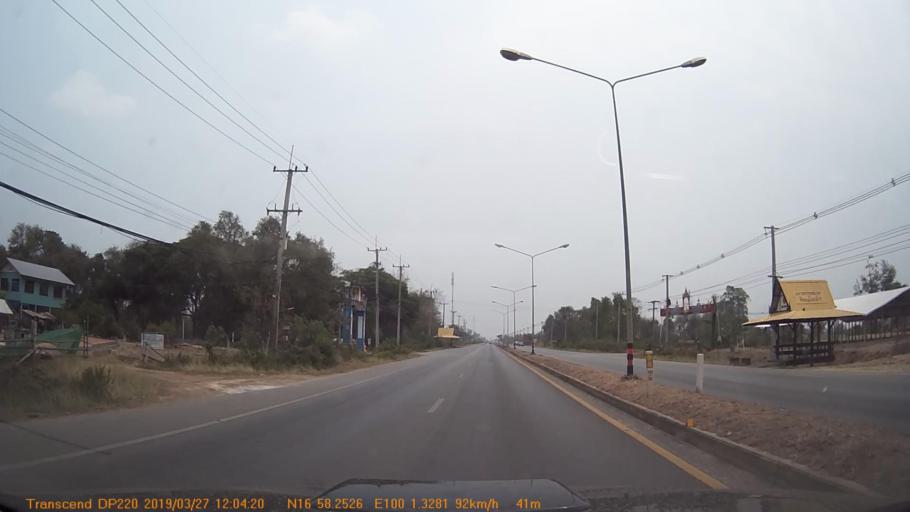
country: TH
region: Sukhothai
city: Kong Krailat
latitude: 16.9709
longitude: 100.0224
